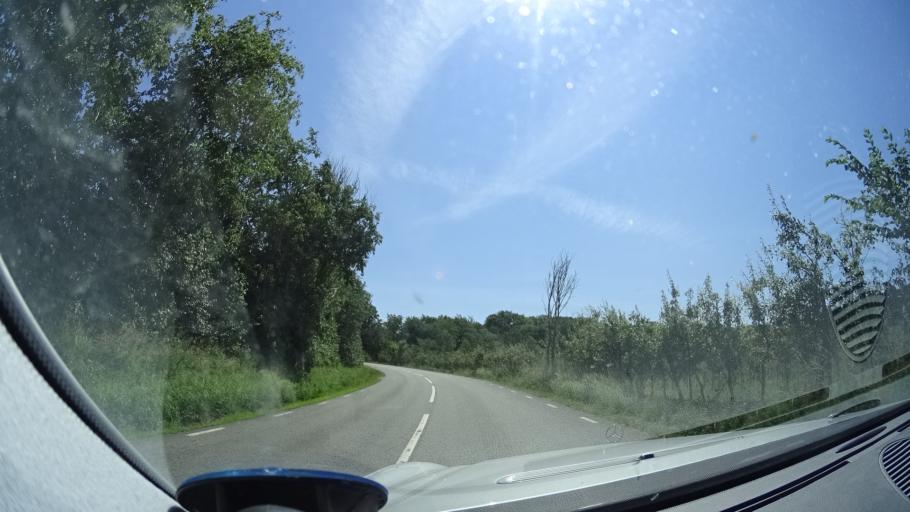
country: SE
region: Skane
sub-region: Kristianstads Kommun
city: Degeberga
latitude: 55.8929
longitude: 14.0029
